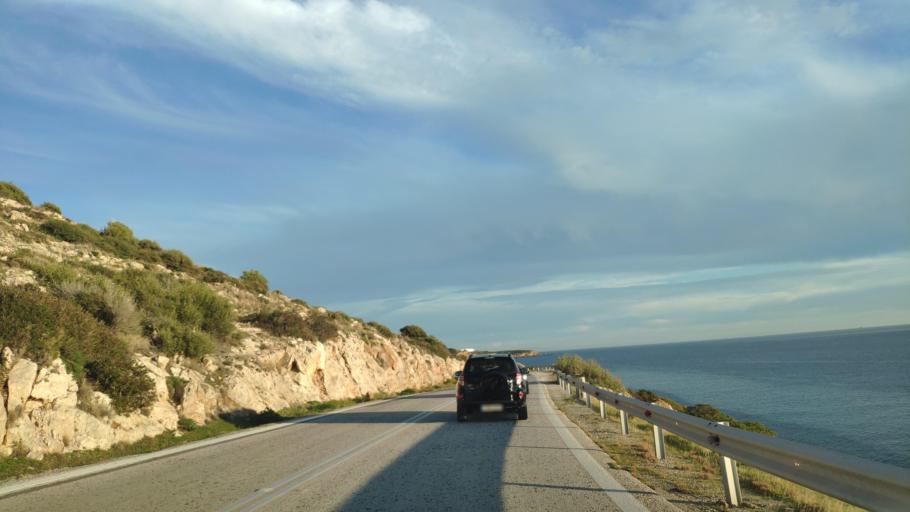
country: GR
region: Attica
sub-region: Nomarchia Anatolikis Attikis
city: Palaia Fokaia
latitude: 37.6669
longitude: 23.9611
